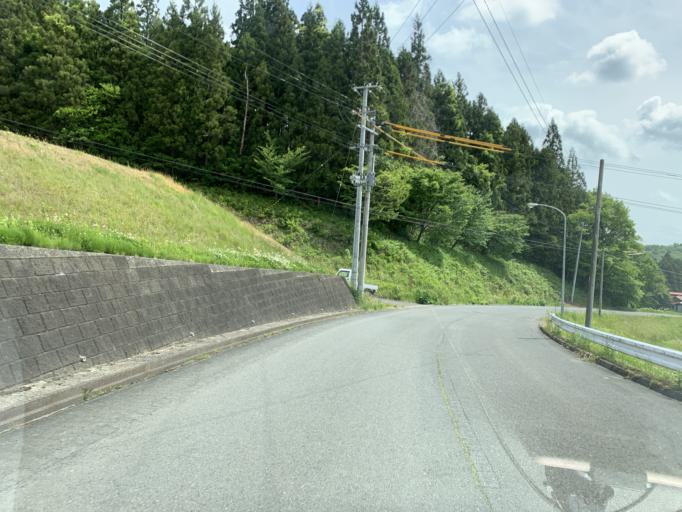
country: JP
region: Iwate
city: Ichinoseki
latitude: 38.8604
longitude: 140.9884
